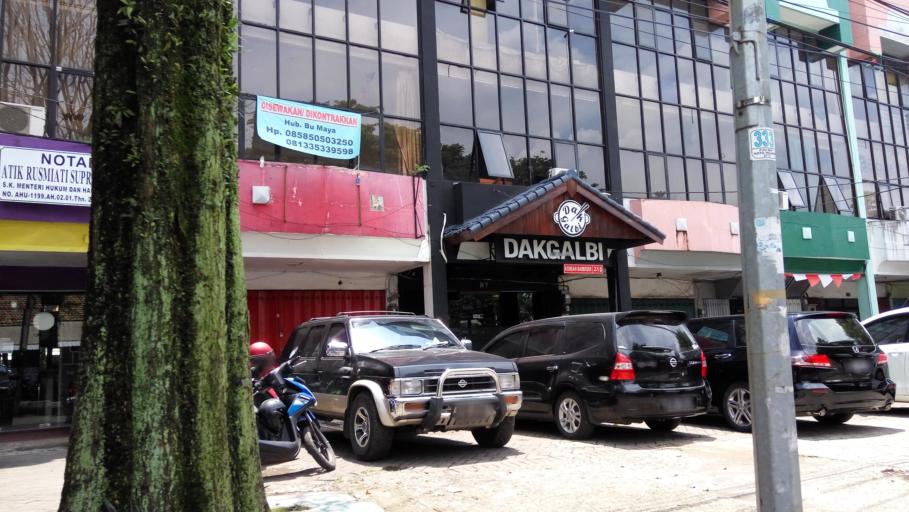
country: ID
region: East Java
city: Malang
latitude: -7.9695
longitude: 112.6177
